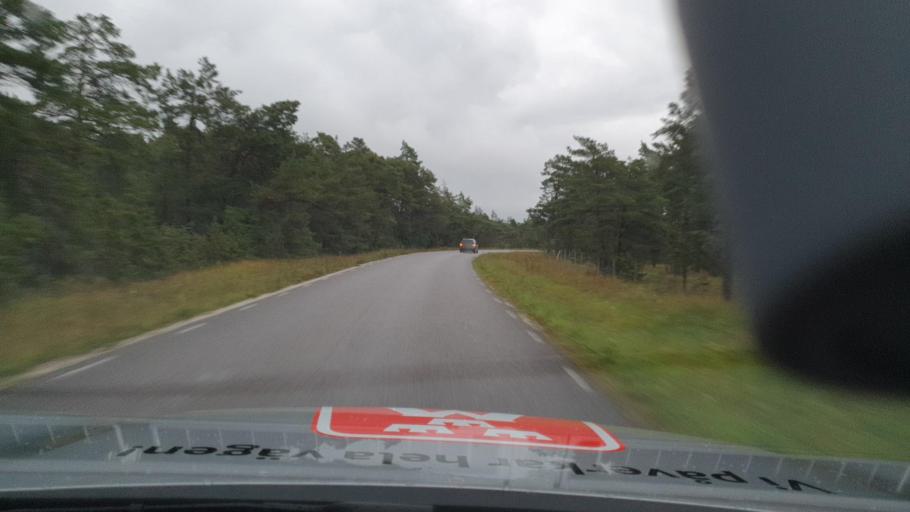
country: SE
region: Gotland
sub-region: Gotland
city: Slite
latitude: 57.7524
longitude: 18.7661
